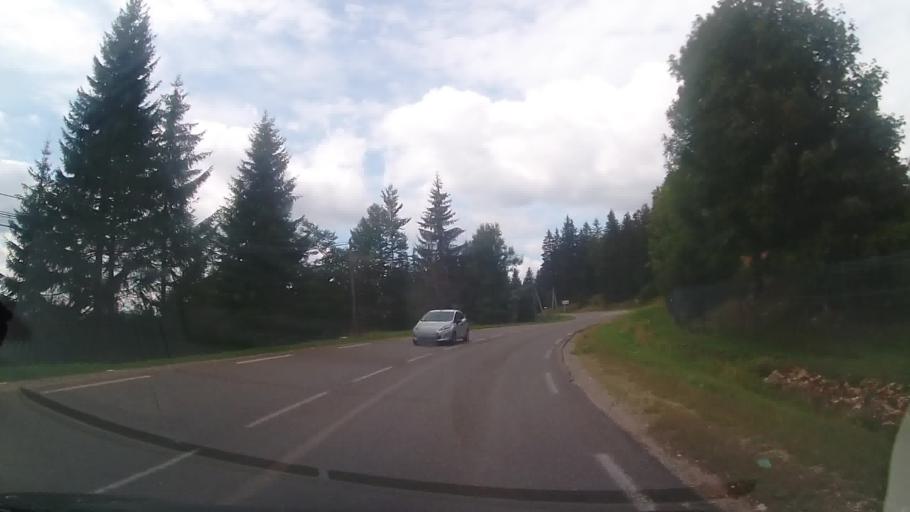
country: FR
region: Franche-Comte
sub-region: Departement du Jura
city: Les Rousses
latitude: 46.4590
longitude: 6.0738
